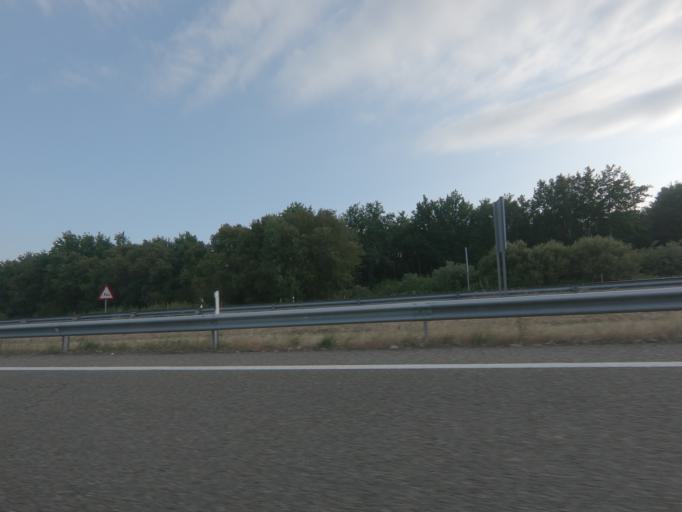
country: ES
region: Galicia
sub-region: Provincia de Ourense
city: Allariz
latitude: 42.1984
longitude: -7.7818
